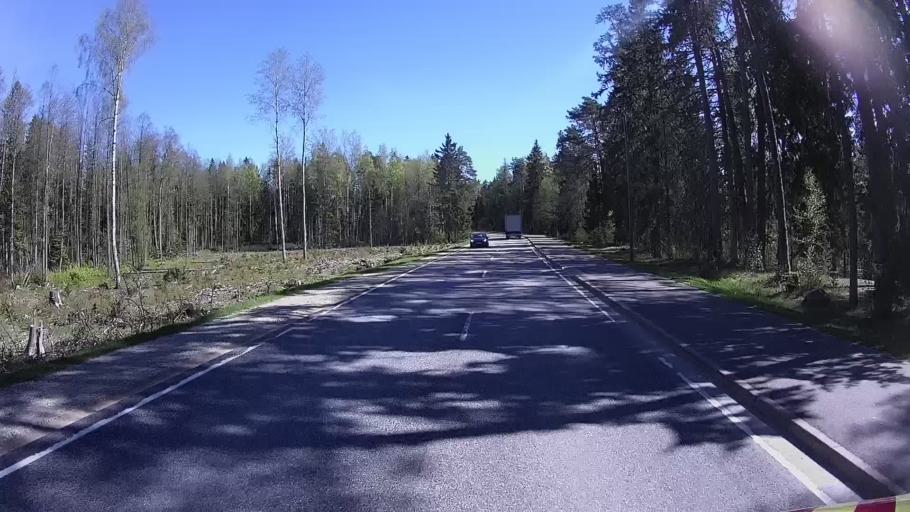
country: EE
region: Harju
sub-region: Kuusalu vald
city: Kuusalu
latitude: 59.2732
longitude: 25.6326
